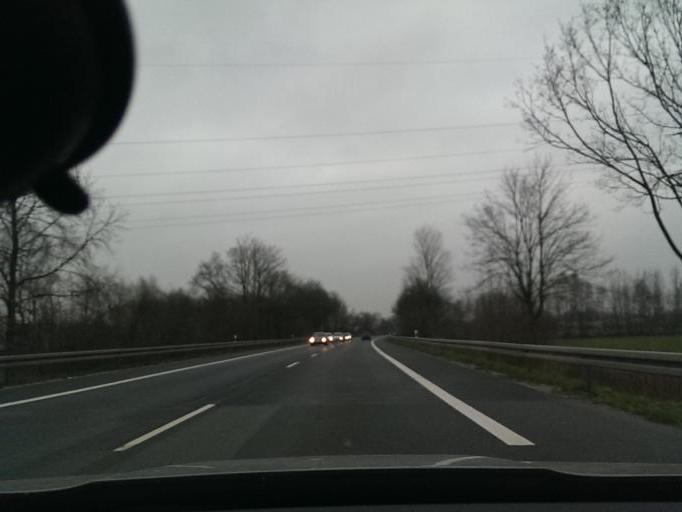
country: DE
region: North Rhine-Westphalia
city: Rietberg
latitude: 51.8137
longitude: 8.4045
